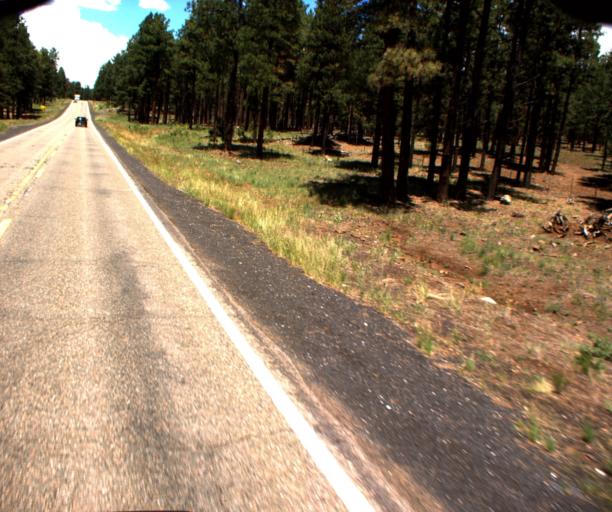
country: US
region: Arizona
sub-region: Coconino County
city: Flagstaff
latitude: 35.2901
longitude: -111.7628
